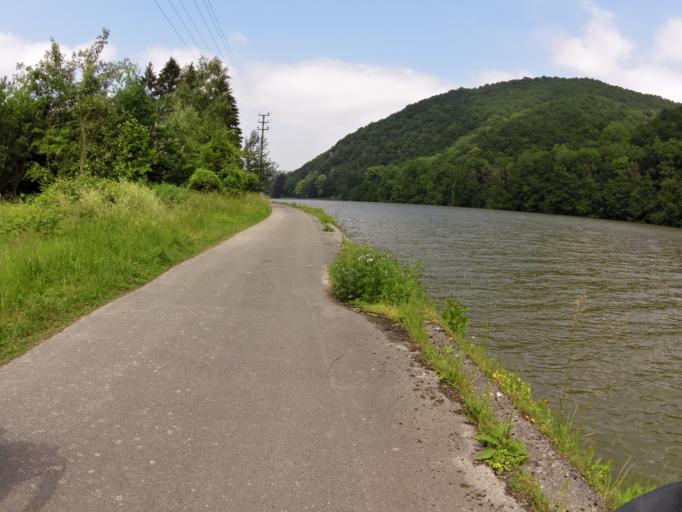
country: BE
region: Wallonia
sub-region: Province de Namur
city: Hastiere-Lavaux
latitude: 50.1926
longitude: 4.8241
